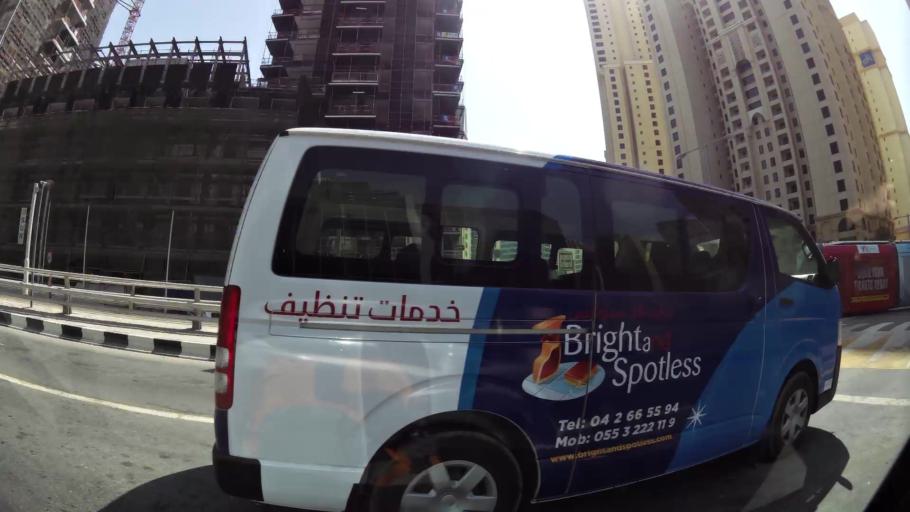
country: AE
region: Dubai
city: Dubai
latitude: 25.0724
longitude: 55.1318
